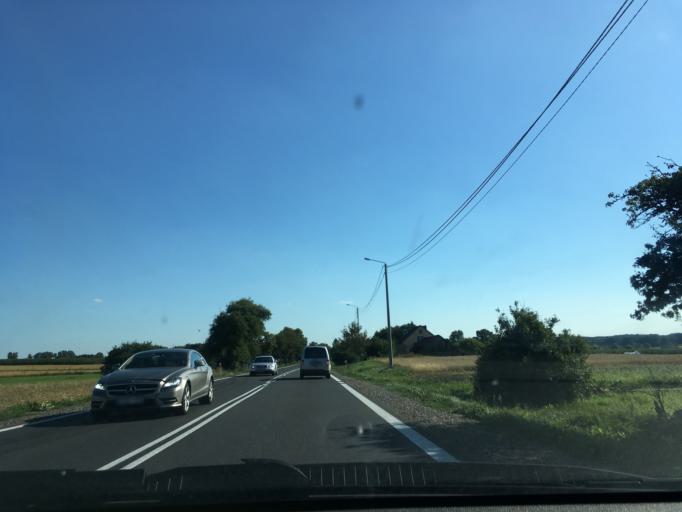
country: PL
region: Podlasie
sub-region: Powiat sokolski
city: Suchowola
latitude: 53.4701
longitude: 23.0901
